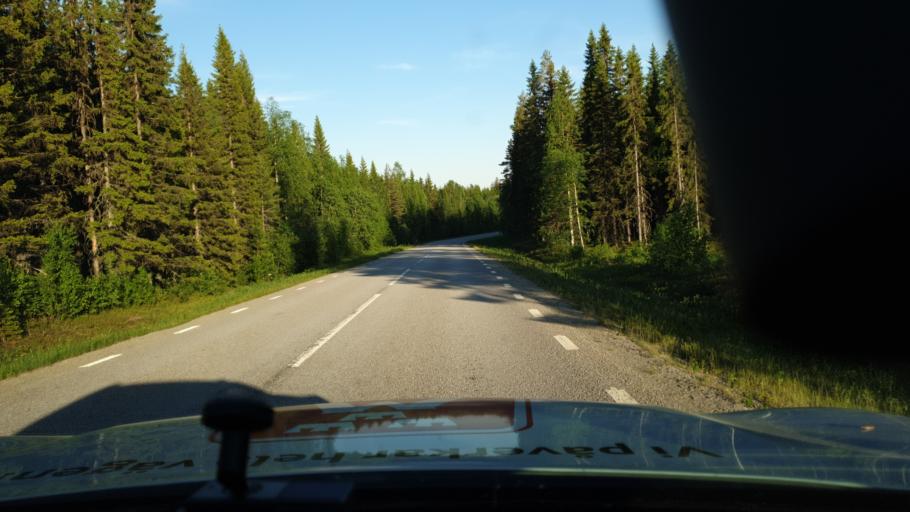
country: SE
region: Vaesterbotten
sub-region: Bjurholms Kommun
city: Bjurholm
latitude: 63.9511
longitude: 19.1800
